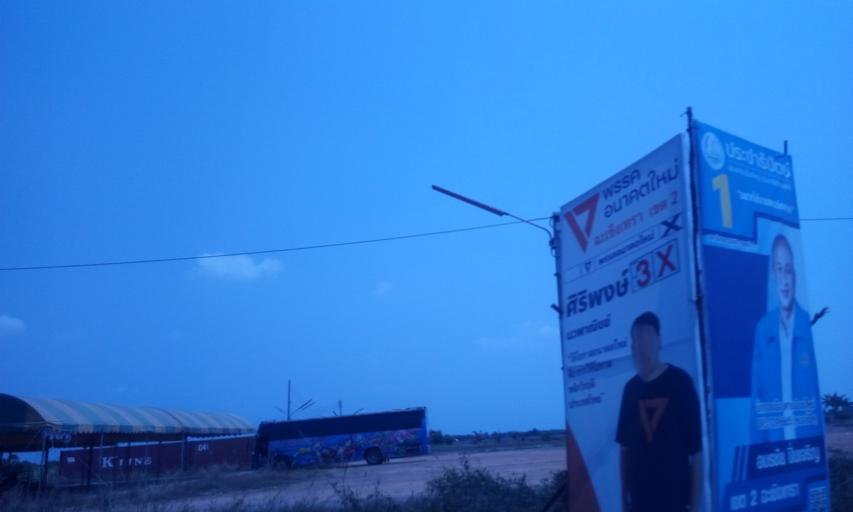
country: TH
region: Chachoengsao
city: Bang Nam Priao
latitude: 13.9628
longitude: 100.9671
